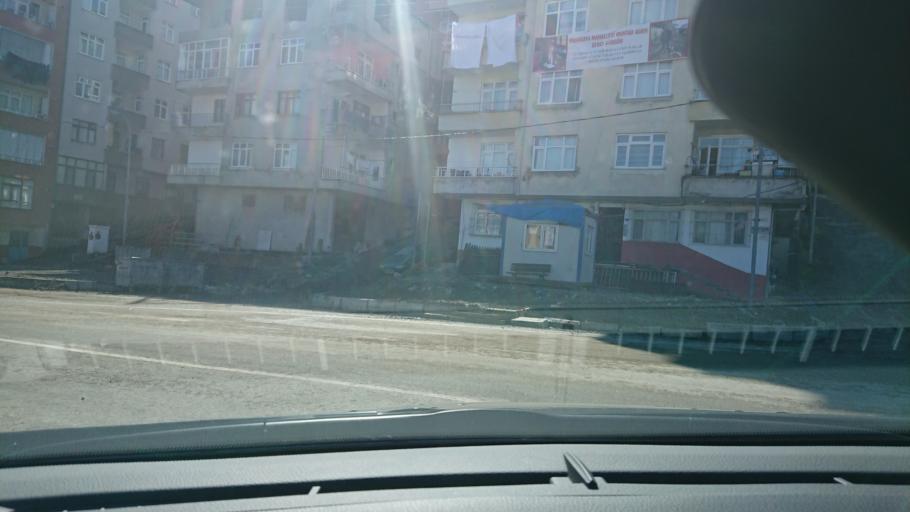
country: TR
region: Rize
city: Rize
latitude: 41.0212
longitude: 40.5282
